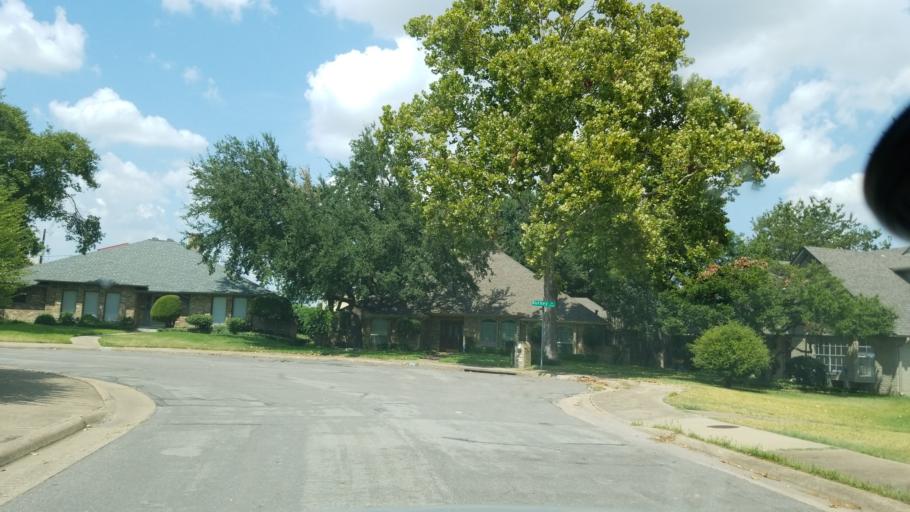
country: US
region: Texas
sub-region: Dallas County
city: Richardson
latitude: 32.9206
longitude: -96.7184
